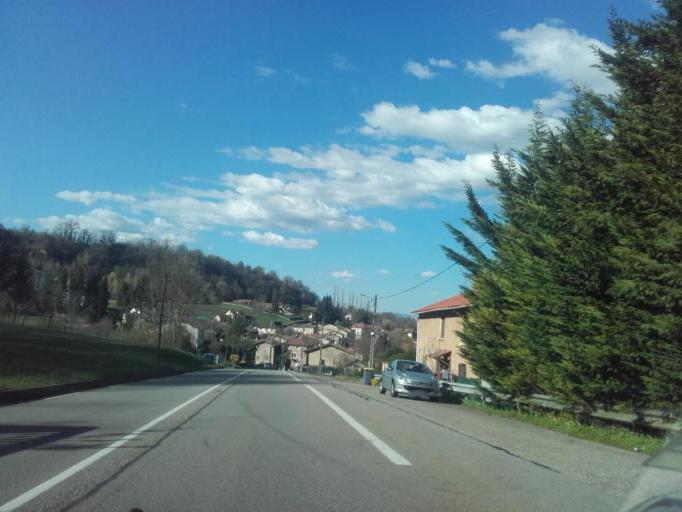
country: FR
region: Rhone-Alpes
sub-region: Departement de l'Isere
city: Nivolas-Vermelle
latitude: 45.5287
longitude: 5.3072
